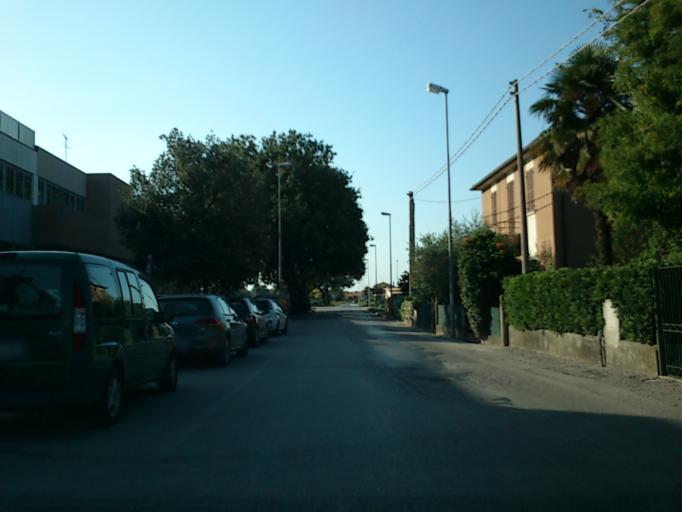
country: IT
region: The Marches
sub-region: Provincia di Pesaro e Urbino
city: Fano
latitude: 43.8282
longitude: 13.0415
